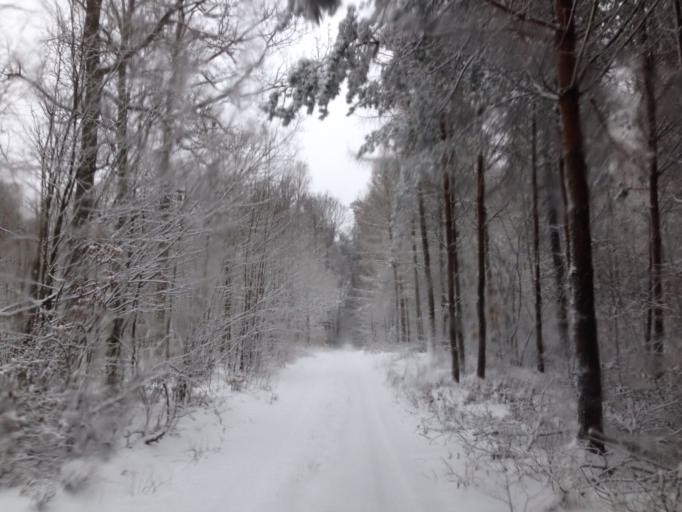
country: PL
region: Kujawsko-Pomorskie
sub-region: Powiat brodnicki
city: Gorzno
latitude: 53.1819
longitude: 19.6839
